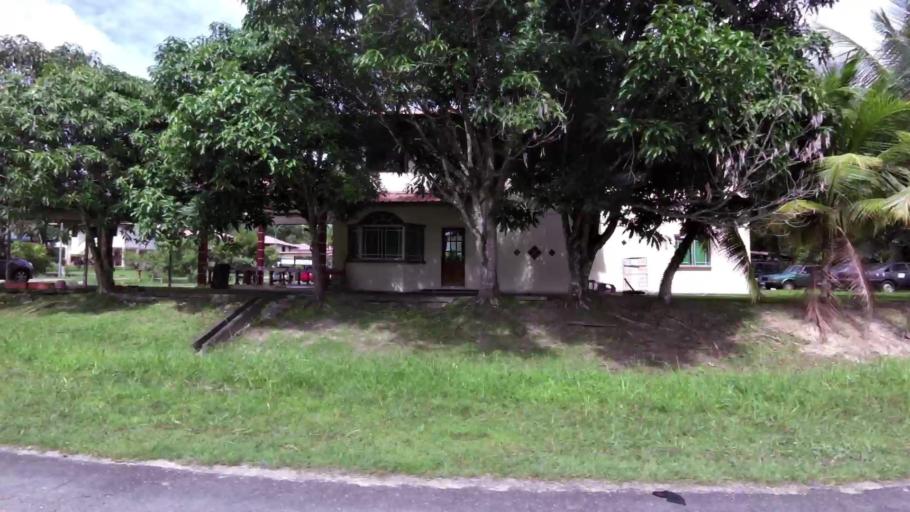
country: BN
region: Brunei and Muara
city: Bandar Seri Begawan
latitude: 4.9333
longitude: 114.9029
